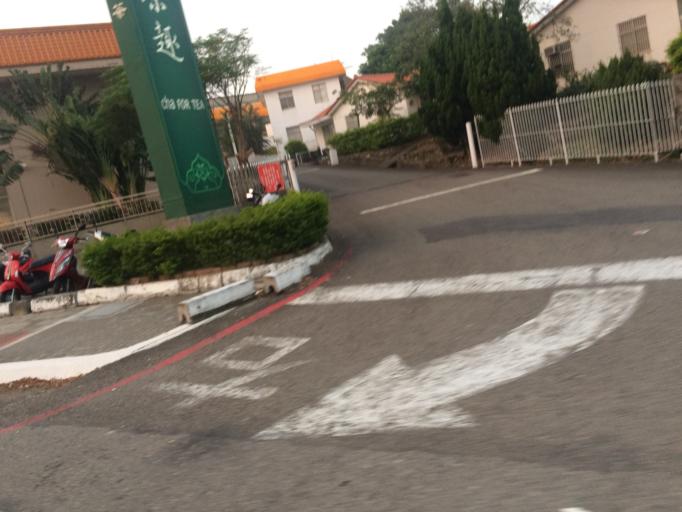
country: TW
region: Taiwan
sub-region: Hsinchu
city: Hsinchu
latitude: 24.7157
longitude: 120.9207
